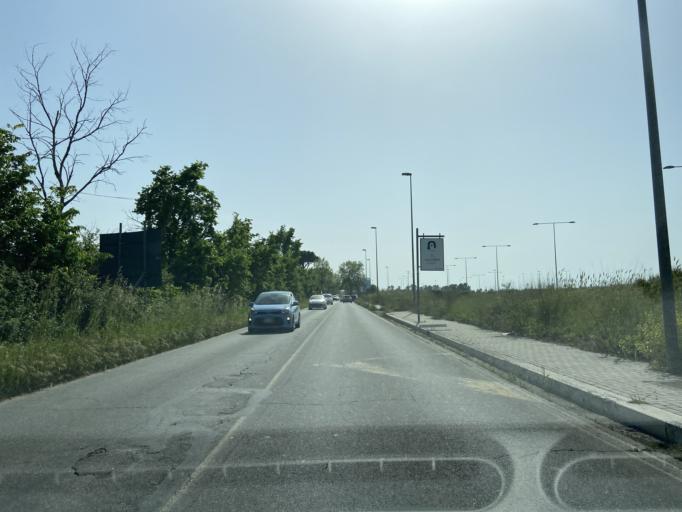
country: IT
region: Latium
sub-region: Citta metropolitana di Roma Capitale
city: Npp 23 (Parco Leonardo)
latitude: 41.7927
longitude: 12.2915
